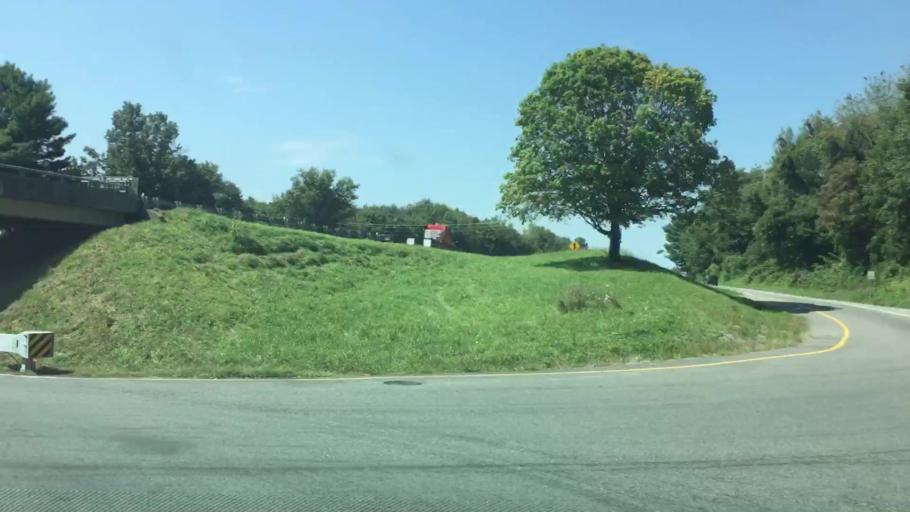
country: US
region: Virginia
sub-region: Washington County
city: Emory
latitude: 36.7581
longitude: -81.8568
